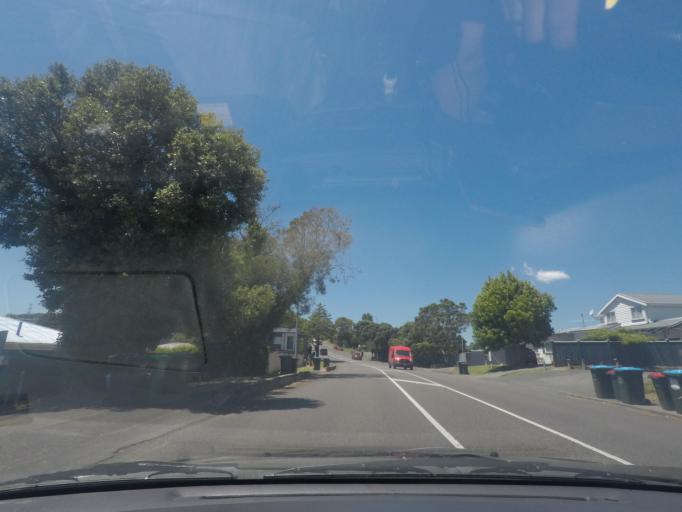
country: NZ
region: Auckland
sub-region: Auckland
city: Mangere
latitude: -36.9286
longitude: 174.7474
